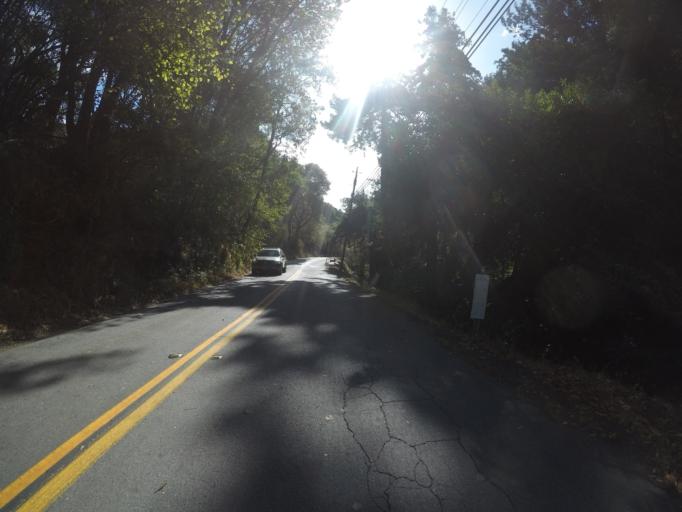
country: US
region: California
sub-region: Santa Cruz County
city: Live Oak
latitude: 36.9961
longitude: -121.9706
